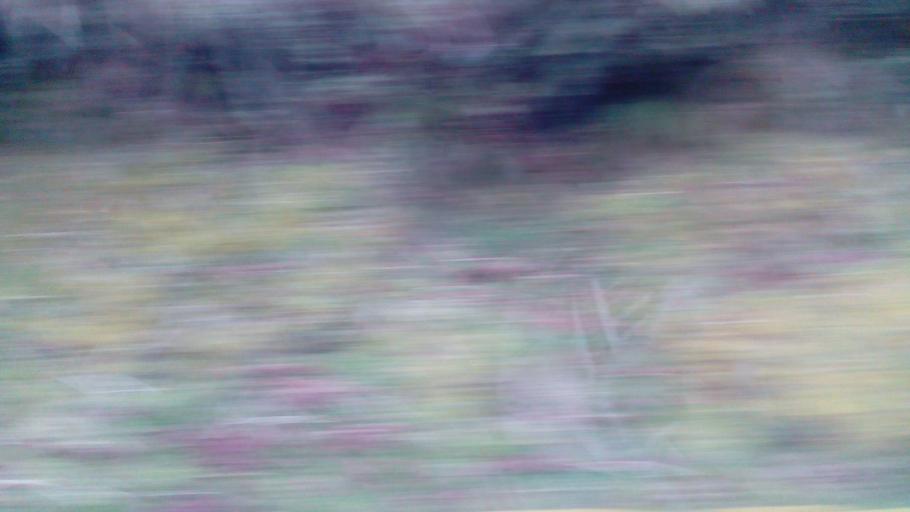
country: TW
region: Taiwan
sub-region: Hualien
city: Hualian
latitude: 24.3812
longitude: 121.3459
